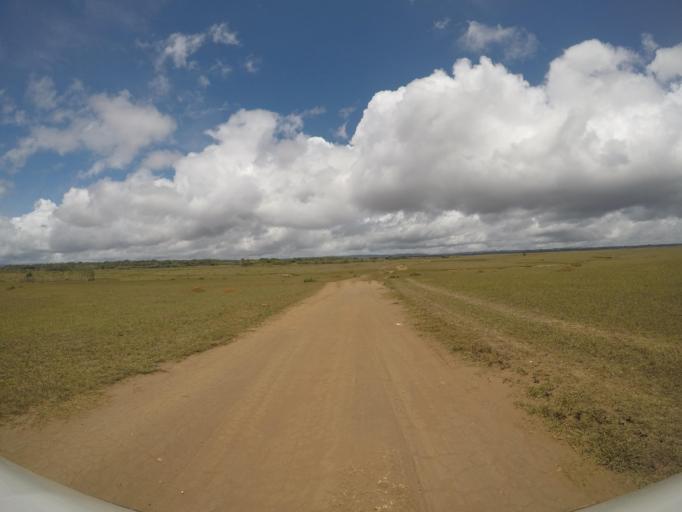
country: TL
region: Lautem
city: Lospalos
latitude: -8.4628
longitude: 126.9847
